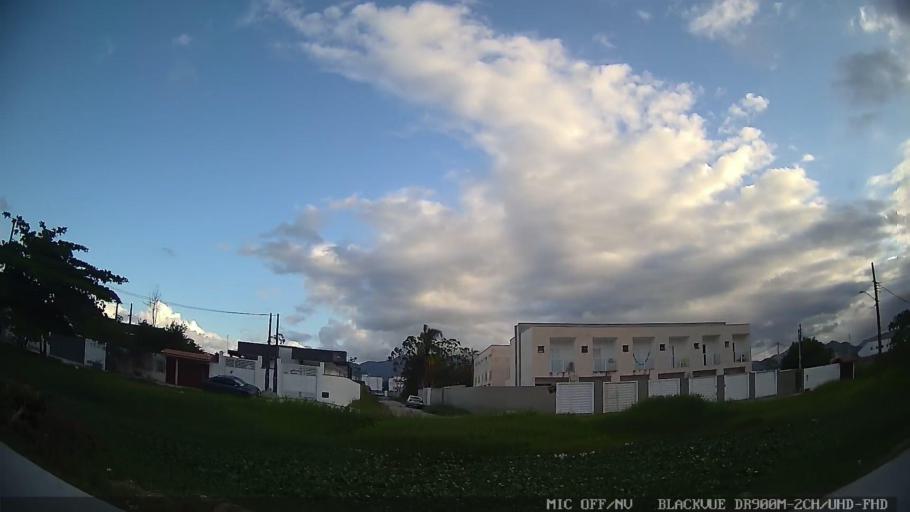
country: BR
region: Sao Paulo
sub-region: Caraguatatuba
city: Caraguatatuba
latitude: -23.6665
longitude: -45.4469
